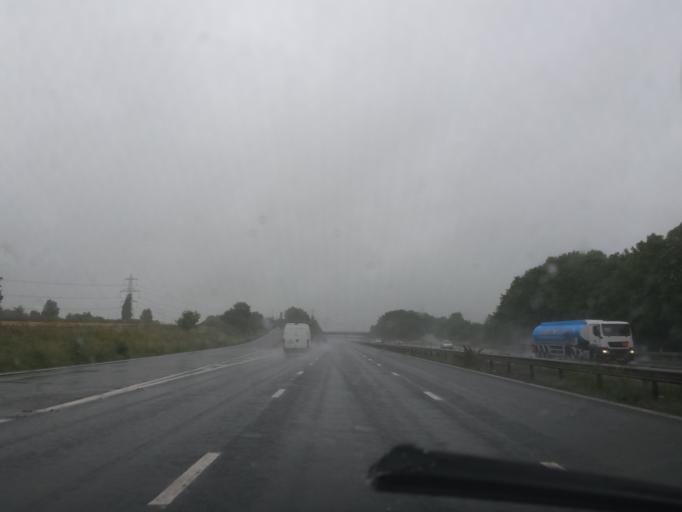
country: GB
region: England
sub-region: Leicestershire
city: Earl Shilton
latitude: 52.5441
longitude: -1.3134
